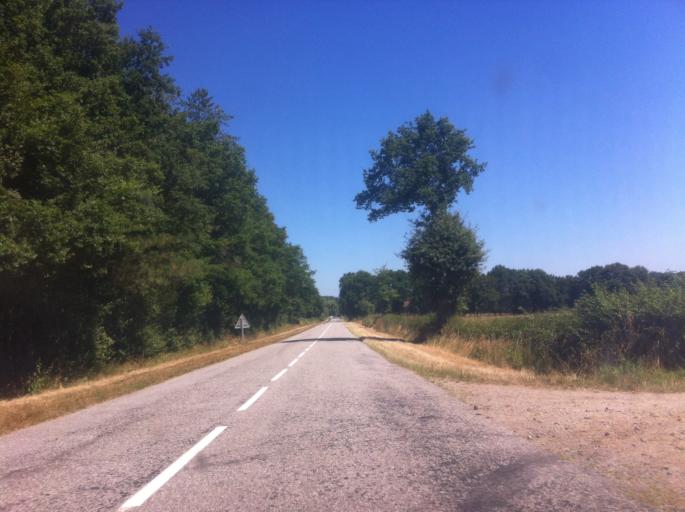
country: FR
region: Auvergne
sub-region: Departement de l'Allier
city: Bellenaves
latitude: 46.2410
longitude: 3.1038
